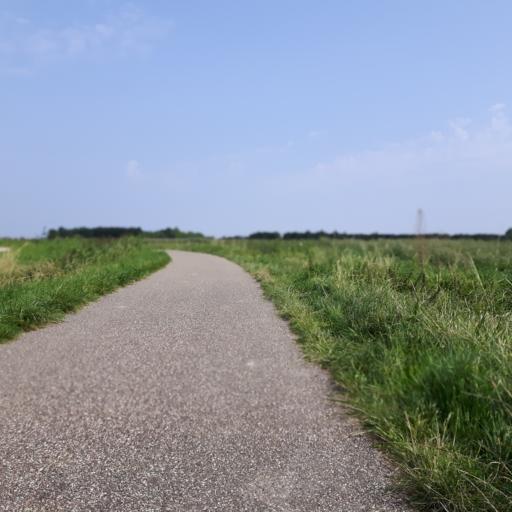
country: NL
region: Zeeland
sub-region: Gemeente Goes
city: Goes
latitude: 51.5062
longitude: 3.9100
